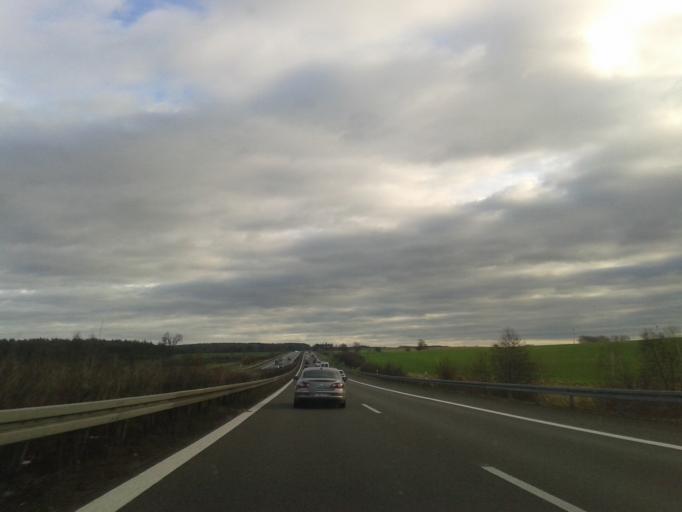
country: DE
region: Saxony
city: Wachau
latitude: 51.1712
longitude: 13.8825
